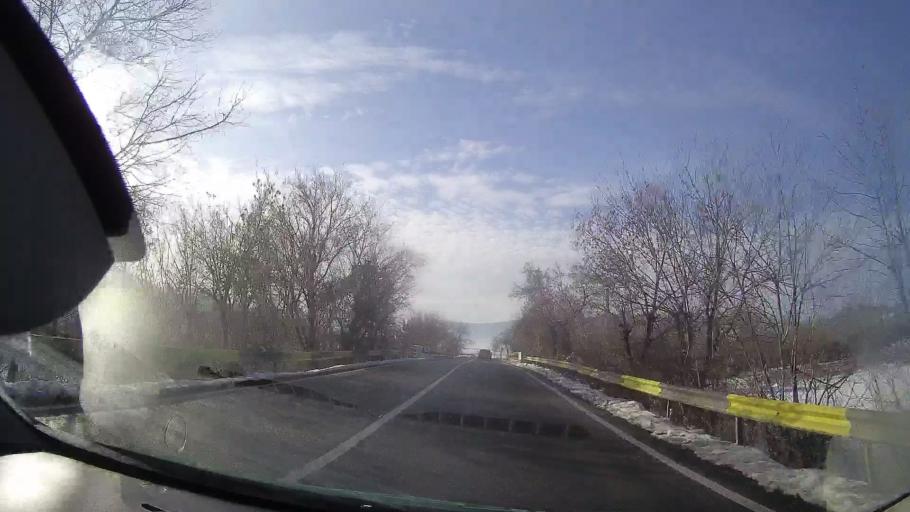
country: RO
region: Neamt
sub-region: Comuna Negresti
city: Negresti
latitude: 46.9979
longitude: 26.3789
